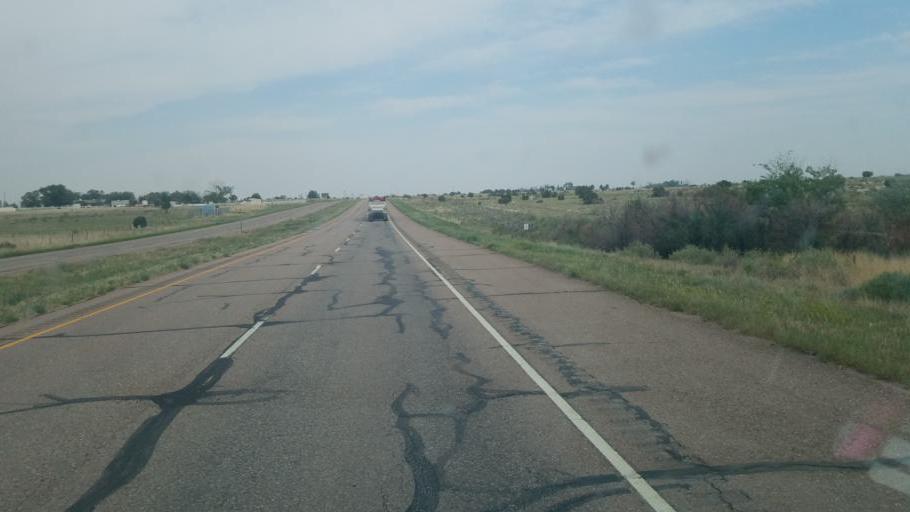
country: US
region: Colorado
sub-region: Fremont County
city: Penrose
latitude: 38.4104
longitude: -105.0110
